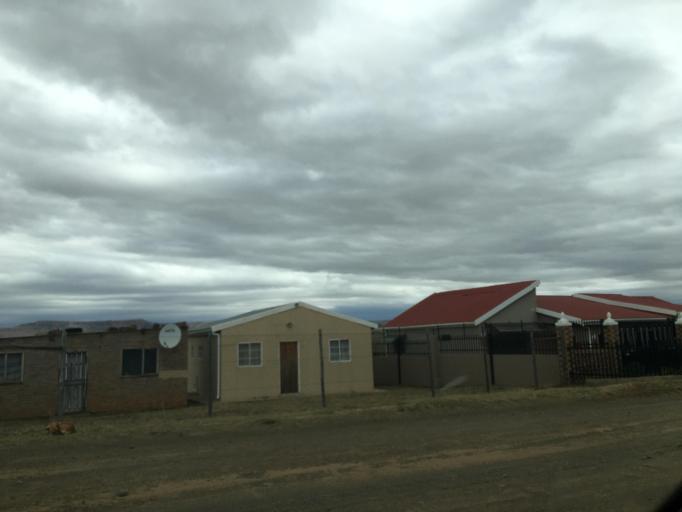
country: ZA
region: Eastern Cape
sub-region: Chris Hani District Municipality
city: Cala
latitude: -31.5404
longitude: 27.6953
